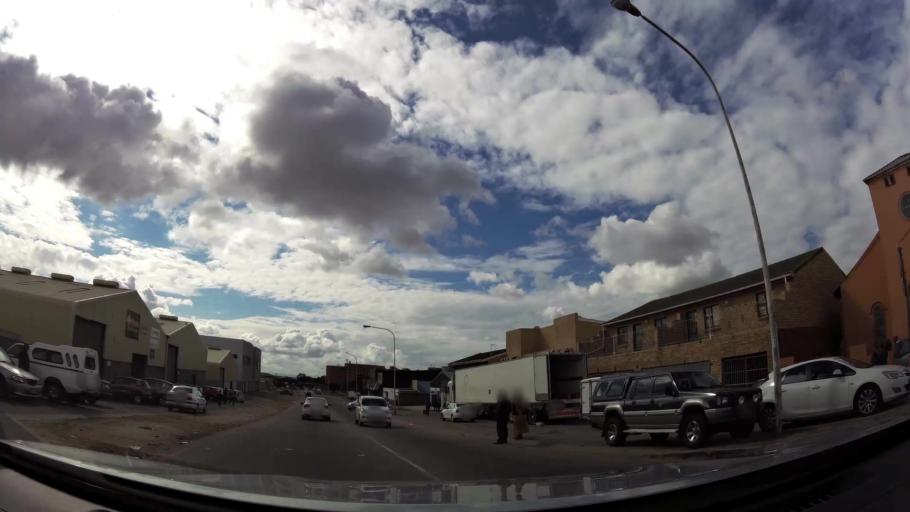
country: ZA
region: Eastern Cape
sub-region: Nelson Mandela Bay Metropolitan Municipality
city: Port Elizabeth
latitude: -33.9271
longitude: 25.5666
